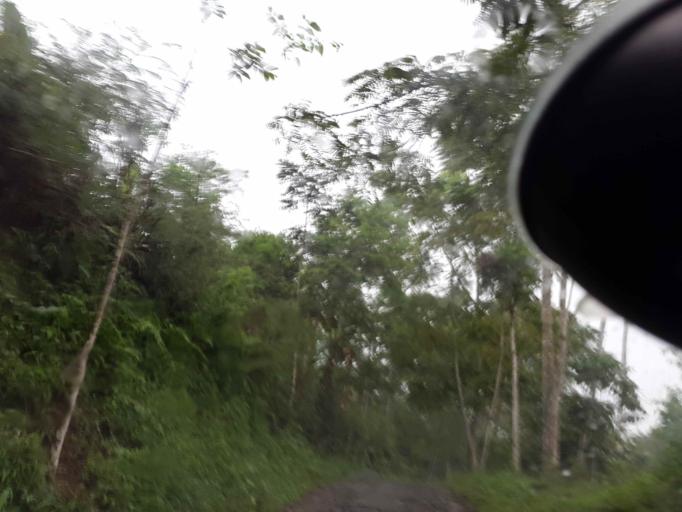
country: ID
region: Central Java
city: Wonosobo
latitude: -7.4499
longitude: 109.9503
